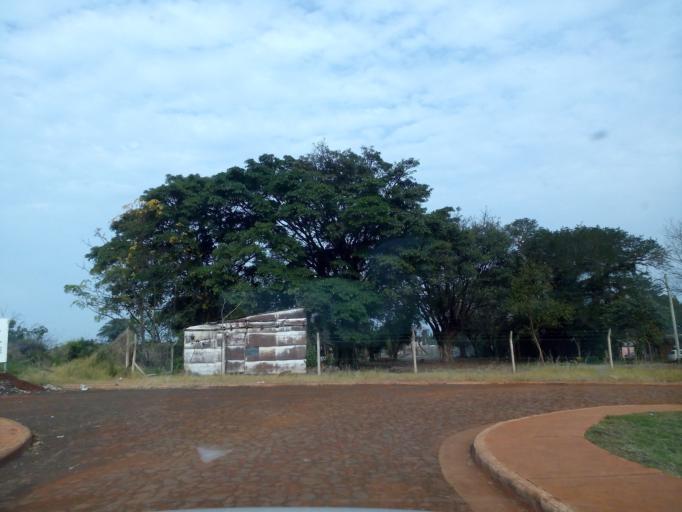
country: AR
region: Misiones
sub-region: Departamento de Capital
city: Posadas
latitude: -27.4213
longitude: -55.8804
